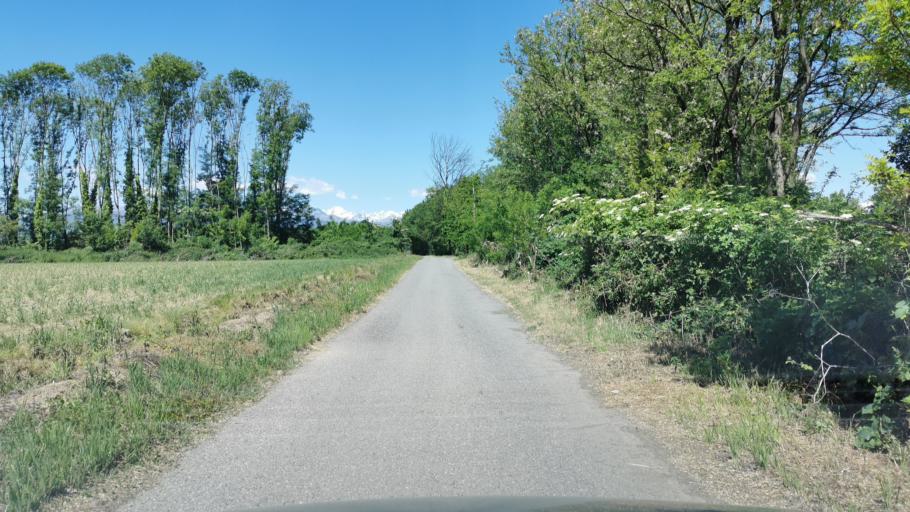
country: IT
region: Piedmont
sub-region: Provincia di Torino
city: Leini
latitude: 45.1715
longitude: 7.7210
